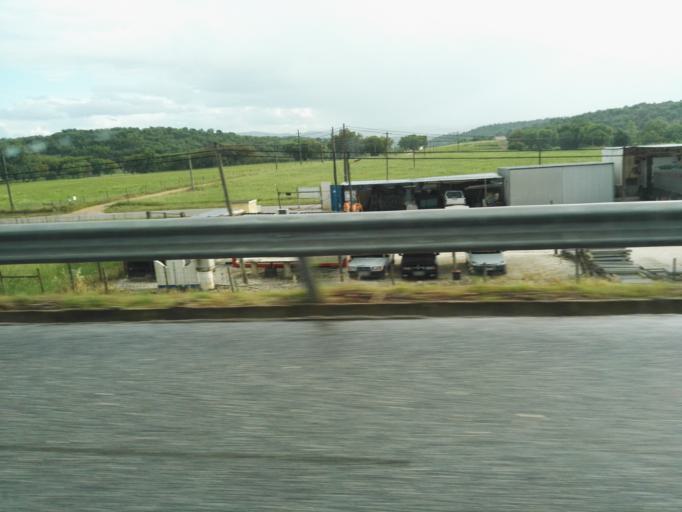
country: PT
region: Evora
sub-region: Estremoz
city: Estremoz
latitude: 38.8197
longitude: -7.5647
